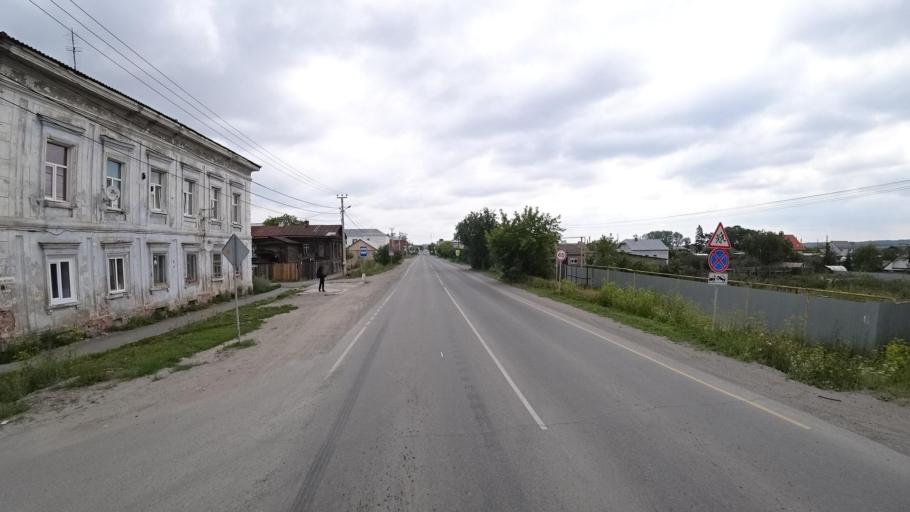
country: RU
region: Sverdlovsk
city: Kamyshlov
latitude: 56.8450
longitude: 62.6948
